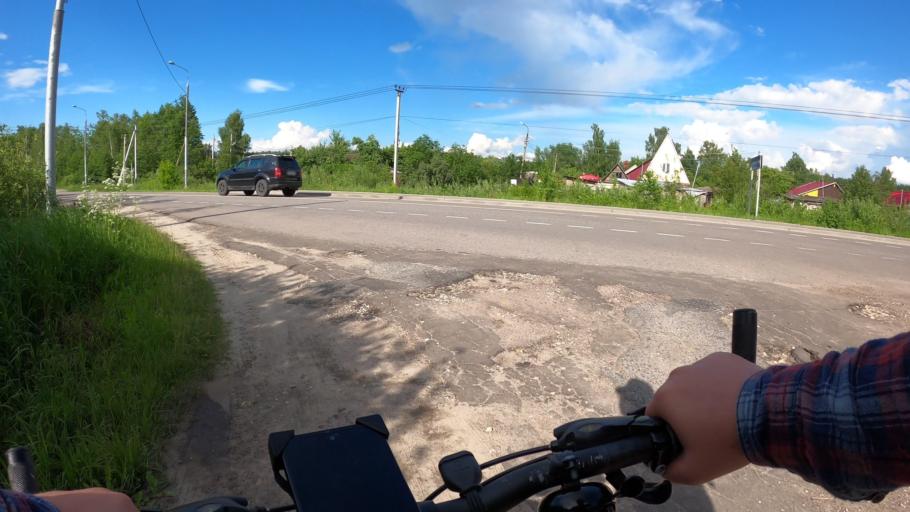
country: RU
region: Moskovskaya
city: Konobeyevo
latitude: 55.4252
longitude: 38.6625
